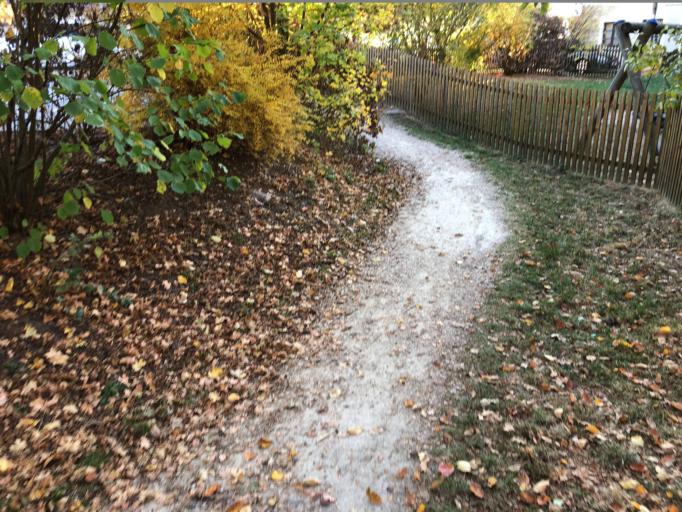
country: DE
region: Bavaria
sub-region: Regierungsbezirk Mittelfranken
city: Feuchtwangen
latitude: 49.1669
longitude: 10.3348
